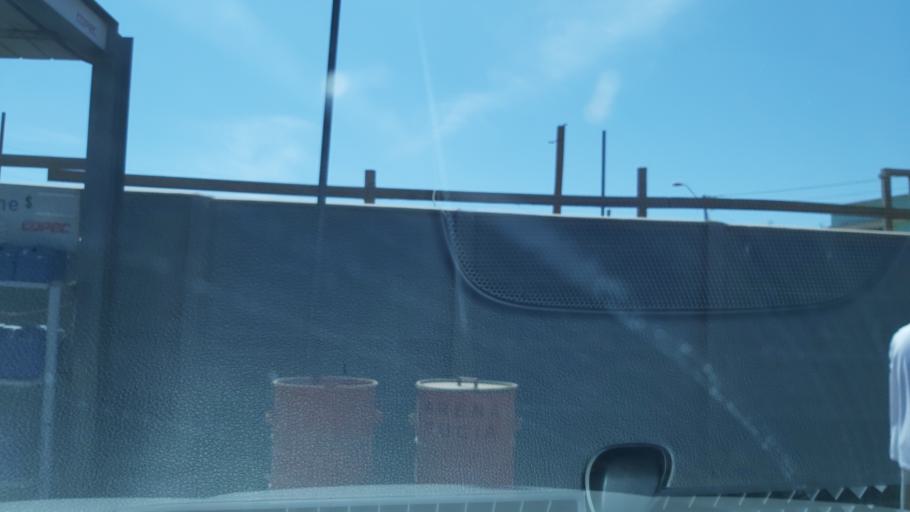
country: CL
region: Atacama
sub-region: Provincia de Chanaral
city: Diego de Almagro
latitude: -26.3902
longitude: -70.0379
